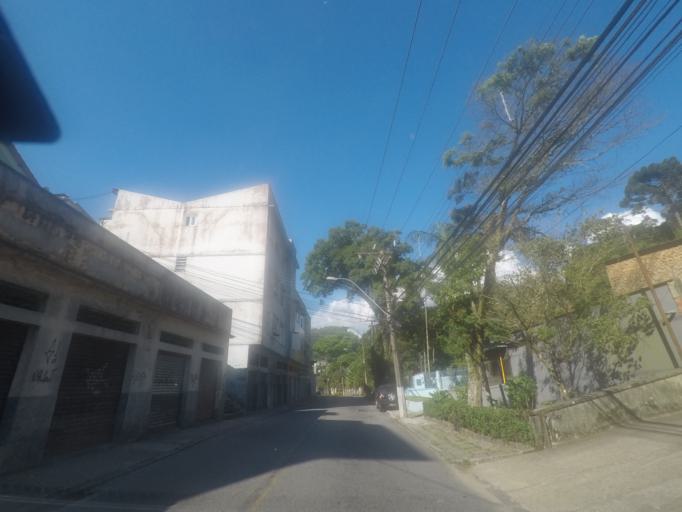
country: BR
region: Rio de Janeiro
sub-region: Petropolis
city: Petropolis
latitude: -22.5254
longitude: -43.1866
